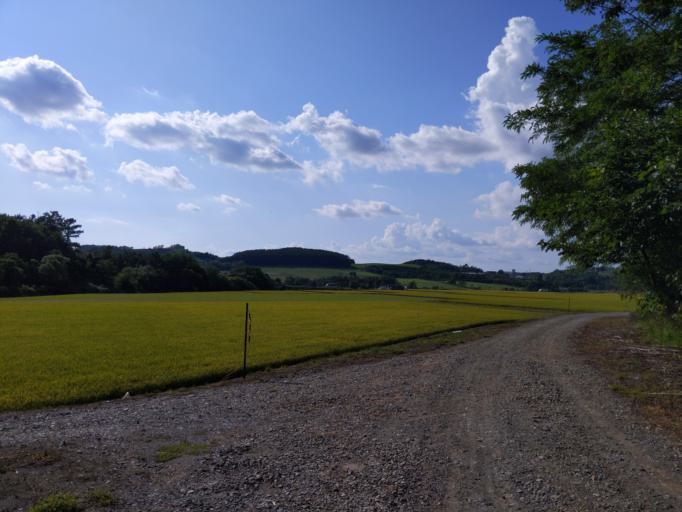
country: JP
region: Hokkaido
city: Iwamizawa
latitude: 43.1908
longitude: 141.8325
